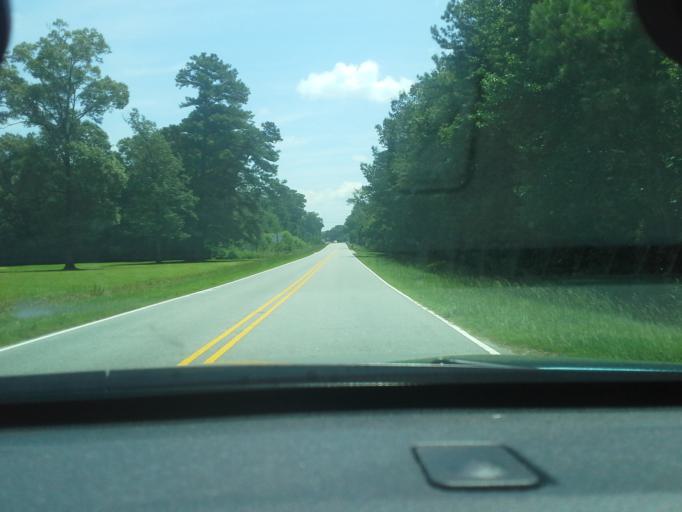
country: US
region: North Carolina
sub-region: Chowan County
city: Edenton
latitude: 35.9308
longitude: -76.6133
